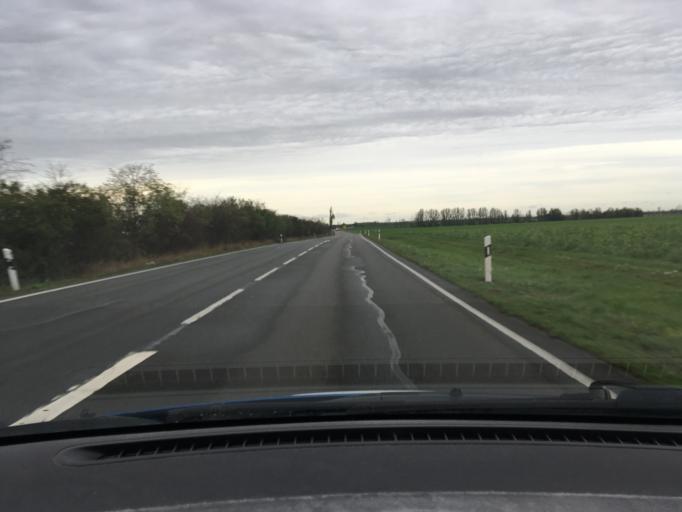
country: DE
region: Saxony-Anhalt
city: Zerbst
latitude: 51.9937
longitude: 12.0402
